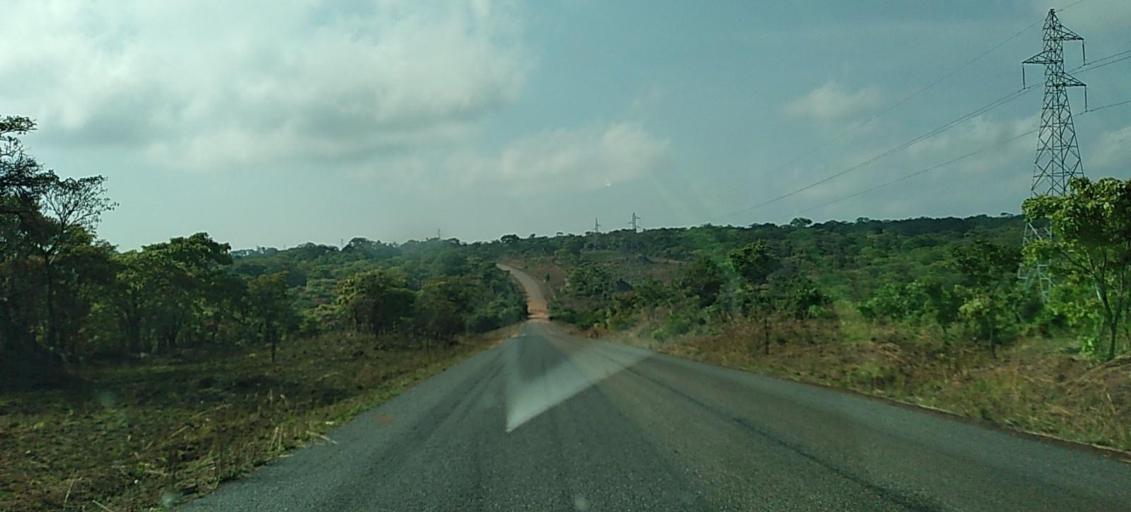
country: ZM
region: North-Western
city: Mwinilunga
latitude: -11.7586
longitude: 24.9958
